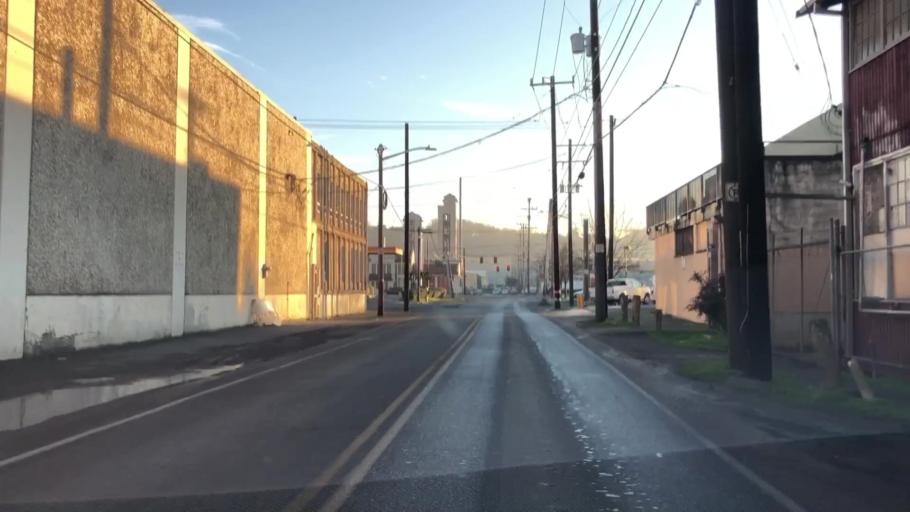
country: US
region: Washington
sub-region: King County
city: Seattle
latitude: 47.5744
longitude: -122.3310
